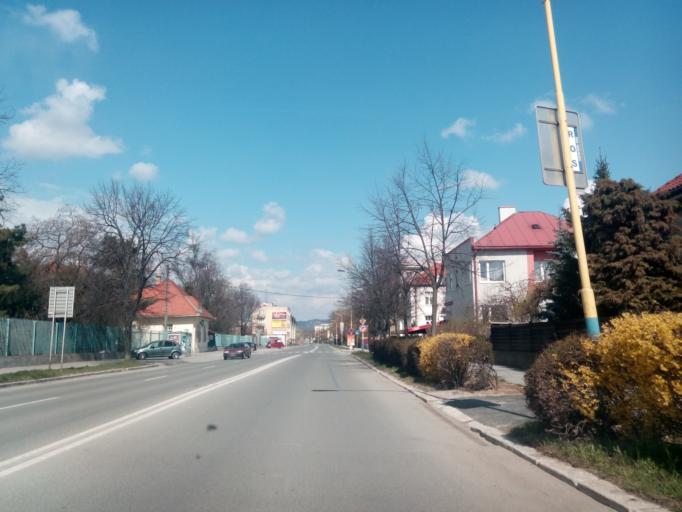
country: SK
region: Kosicky
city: Kosice
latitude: 48.7080
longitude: 21.2576
